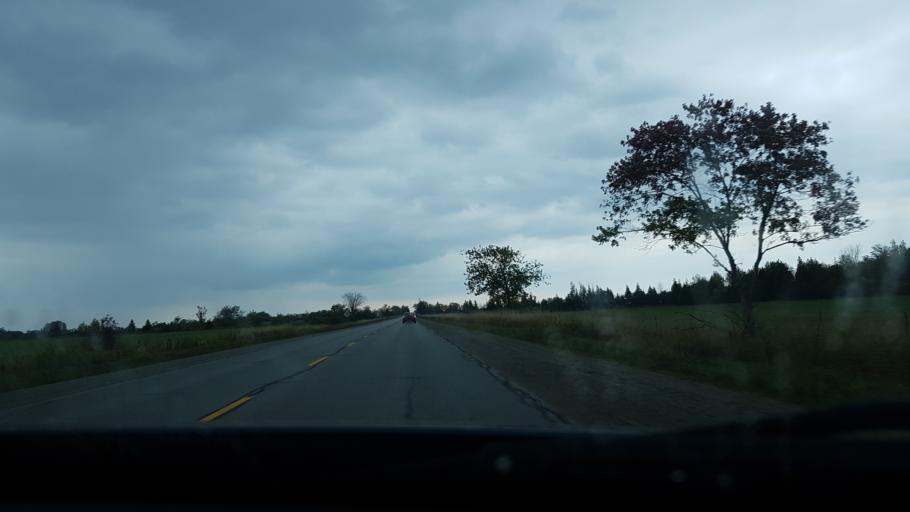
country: CA
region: Ontario
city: Omemee
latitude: 44.3738
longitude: -78.6559
